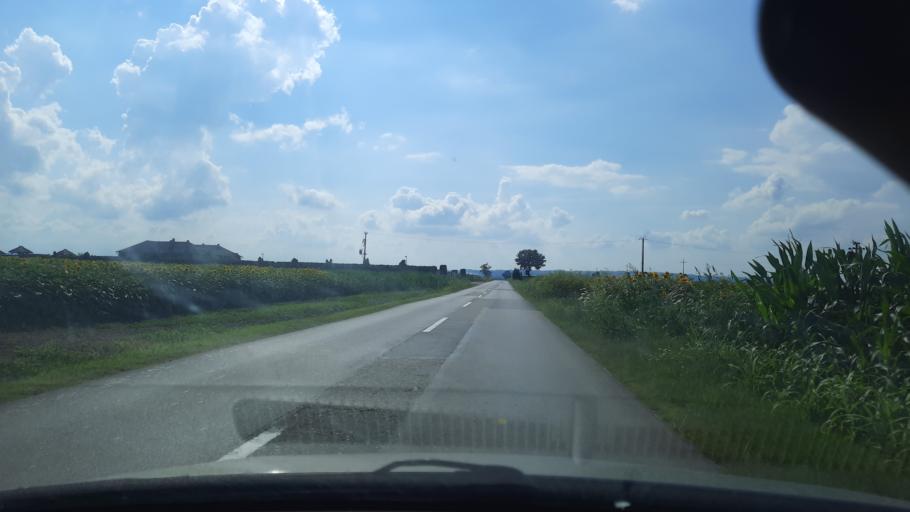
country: RS
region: Central Serbia
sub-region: Branicevski Okrug
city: Malo Crnice
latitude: 44.5831
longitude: 21.3035
